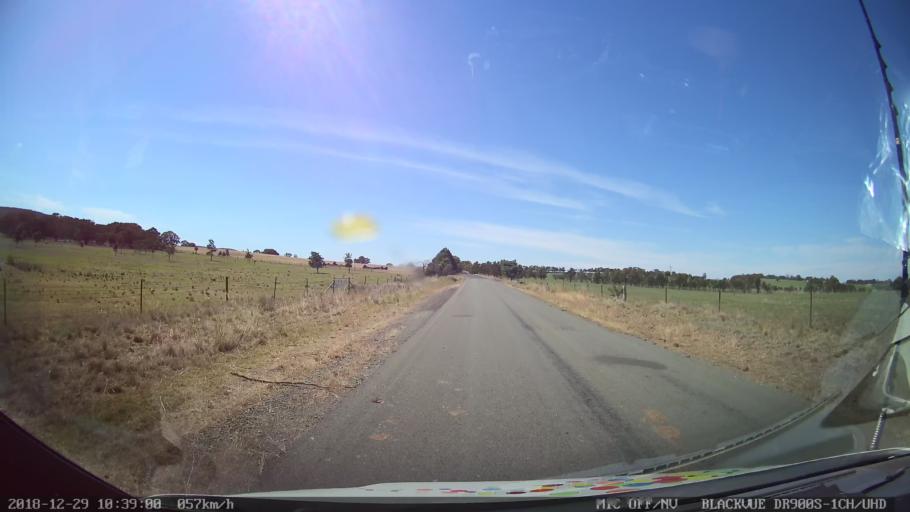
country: AU
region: New South Wales
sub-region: Yass Valley
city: Gundaroo
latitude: -35.0023
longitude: 149.5084
